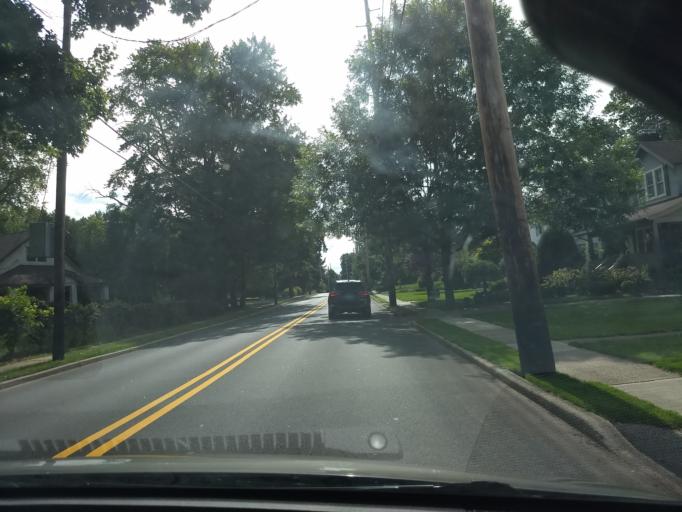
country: US
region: New Jersey
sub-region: Bergen County
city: Glen Rock
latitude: 40.9582
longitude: -74.1314
